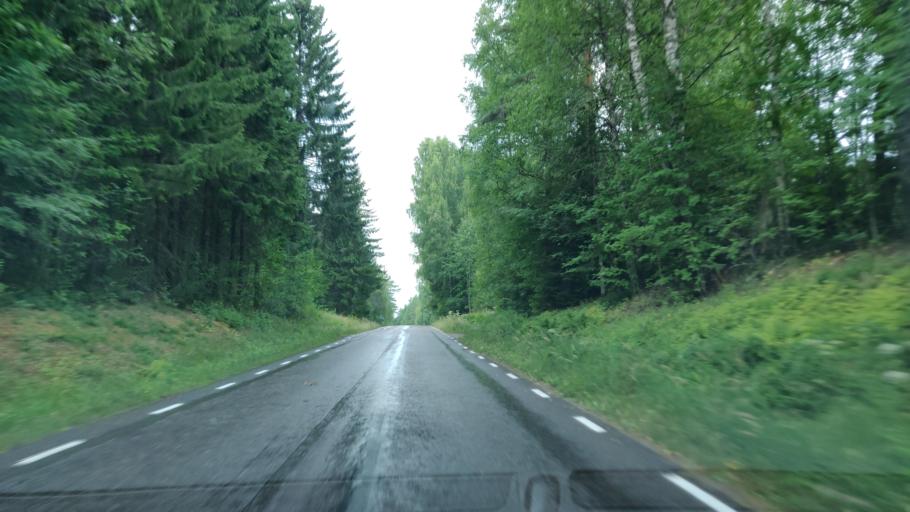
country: SE
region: Vaermland
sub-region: Munkfors Kommun
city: Munkfors
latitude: 59.8765
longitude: 13.5227
